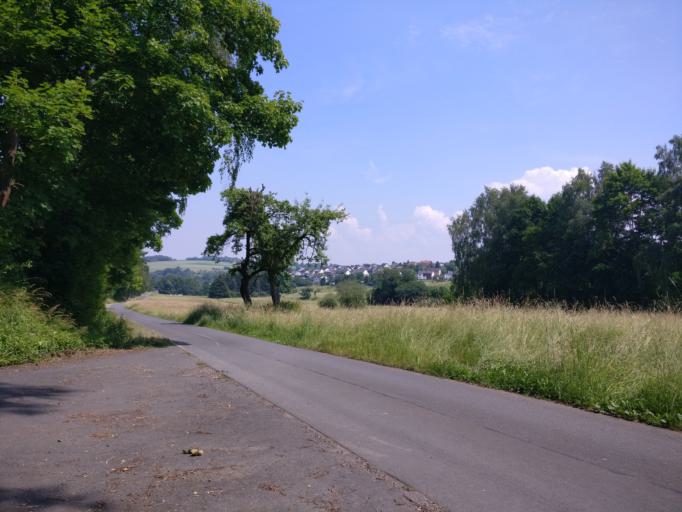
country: DE
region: Hesse
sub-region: Regierungsbezirk Giessen
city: Weinbach
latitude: 50.3968
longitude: 8.3234
